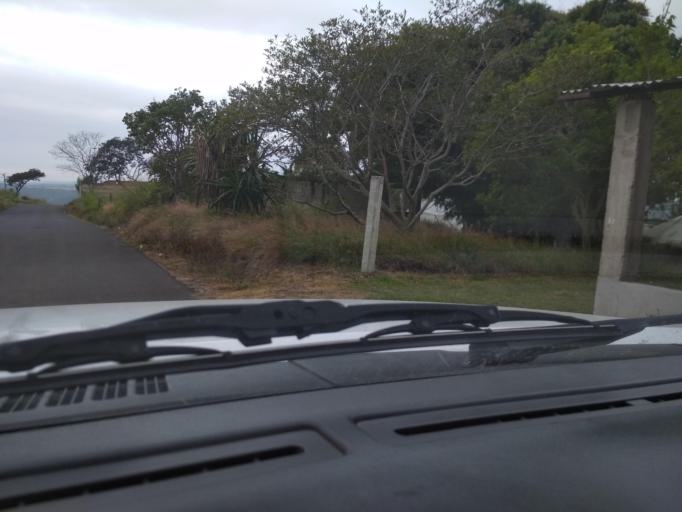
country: MX
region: Veracruz
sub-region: Emiliano Zapata
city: Dos Rios
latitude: 19.5171
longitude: -96.7932
